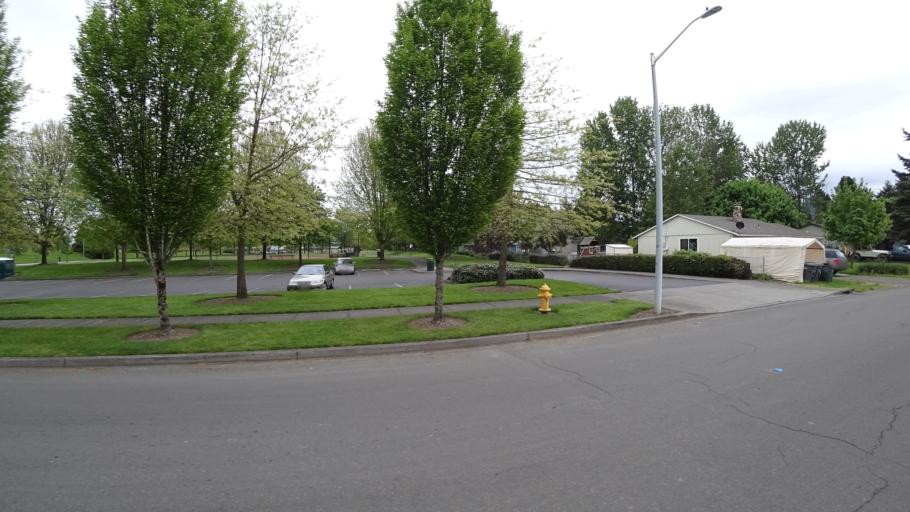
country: US
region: Oregon
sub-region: Washington County
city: Hillsboro
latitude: 45.5393
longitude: -122.9664
